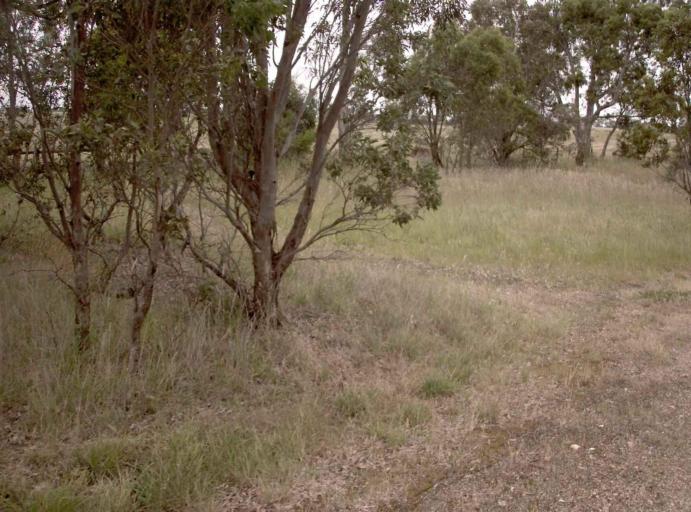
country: AU
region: Victoria
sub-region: Wellington
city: Sale
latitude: -37.9620
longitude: 147.1242
